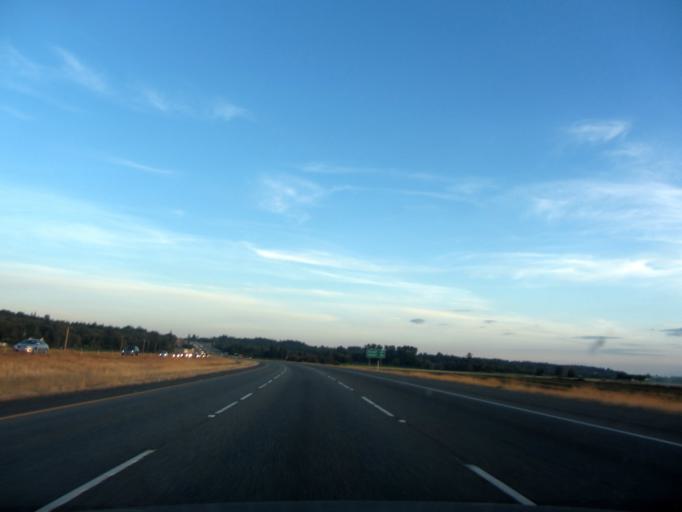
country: US
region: Washington
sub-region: Skagit County
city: Mount Vernon
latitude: 48.3313
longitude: -122.3335
